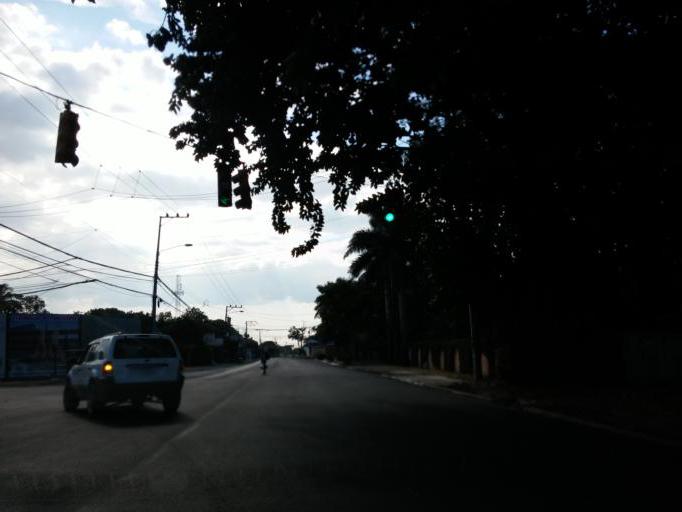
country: CR
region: Heredia
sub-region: Canton de Belen
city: San Antonio
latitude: 9.9785
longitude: -84.1990
